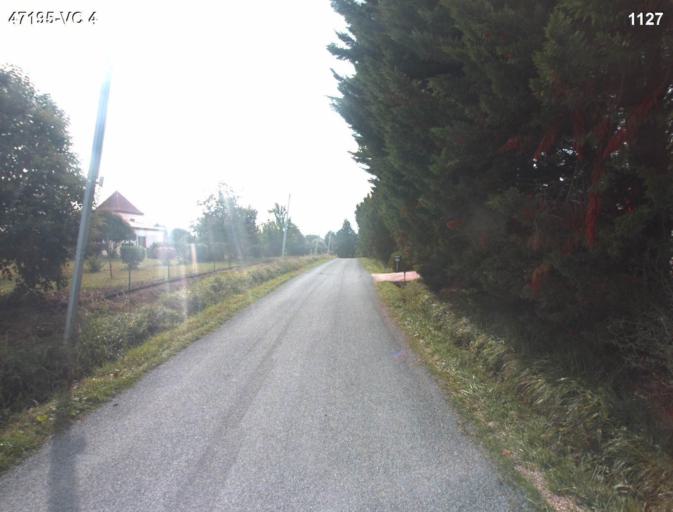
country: FR
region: Aquitaine
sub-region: Departement du Lot-et-Garonne
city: Nerac
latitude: 44.1117
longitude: 0.3819
